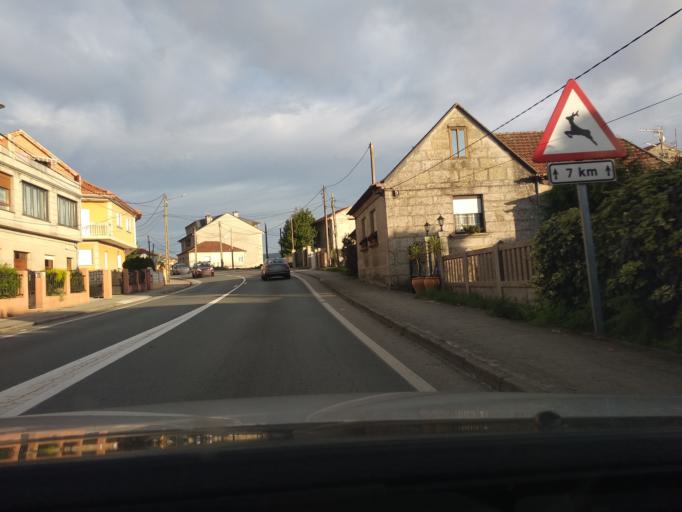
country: ES
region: Galicia
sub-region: Provincia de Pontevedra
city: Moana
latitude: 42.2867
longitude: -8.7241
